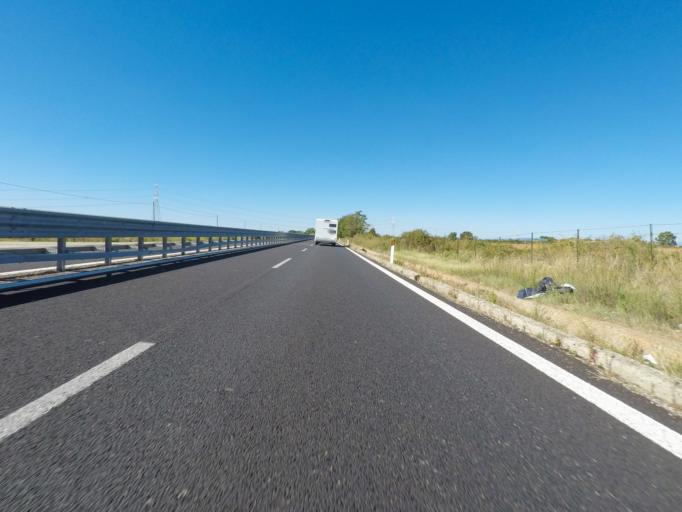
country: IT
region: Latium
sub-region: Provincia di Viterbo
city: Tarquinia
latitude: 42.2757
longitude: 11.7052
